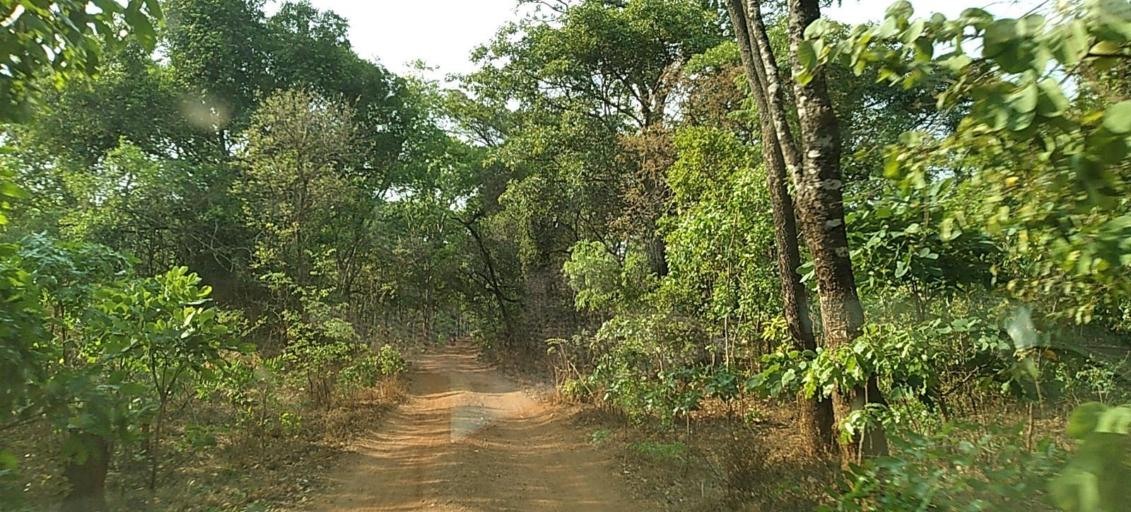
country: ZM
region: Copperbelt
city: Kalulushi
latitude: -12.9680
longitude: 27.7136
